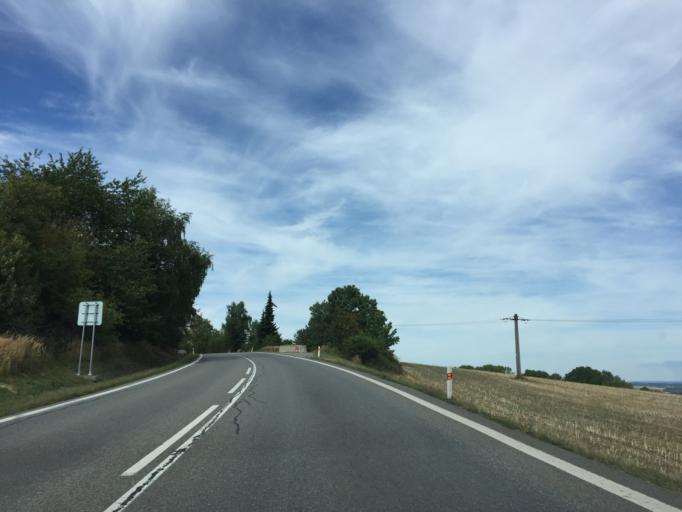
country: CZ
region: Jihocesky
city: Chotoviny
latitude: 49.5536
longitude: 14.6663
